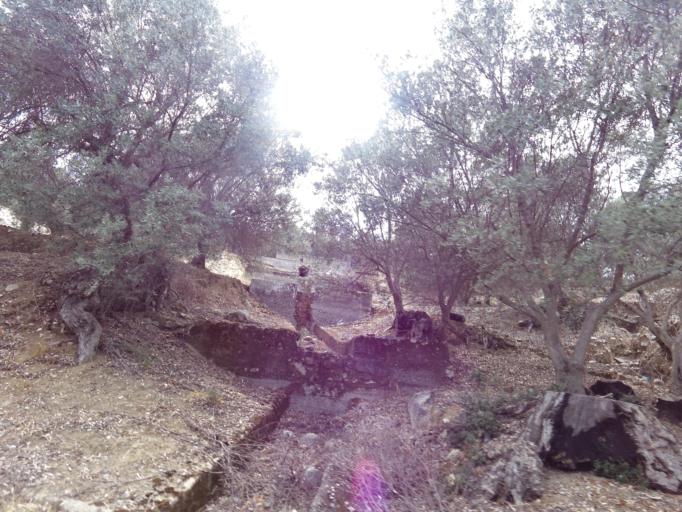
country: IT
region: Calabria
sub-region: Provincia di Reggio Calabria
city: Camini
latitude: 38.4599
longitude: 16.5056
